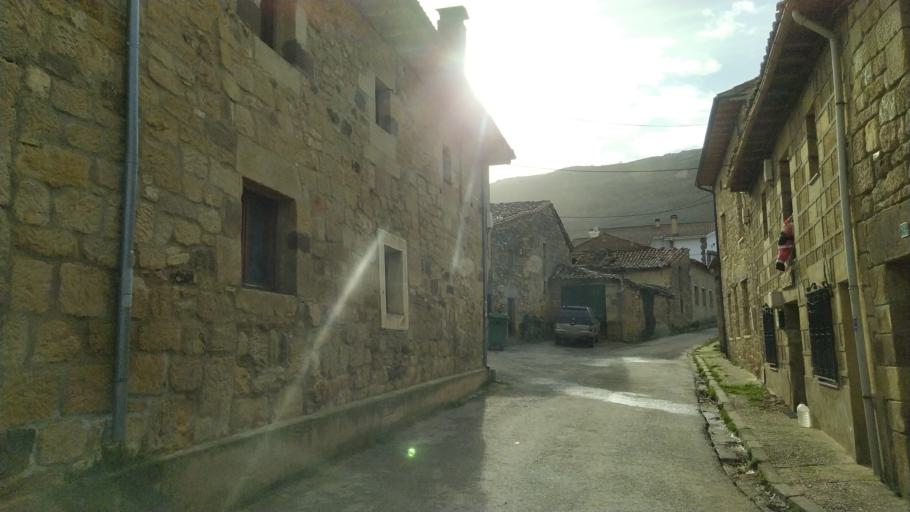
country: ES
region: Cantabria
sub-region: Provincia de Cantabria
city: San Martin de Elines
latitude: 42.8322
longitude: -3.8606
